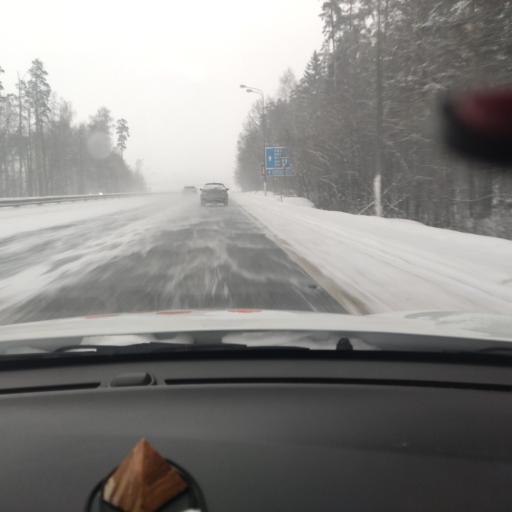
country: RU
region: Tatarstan
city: Osinovo
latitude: 55.8512
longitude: 48.8536
